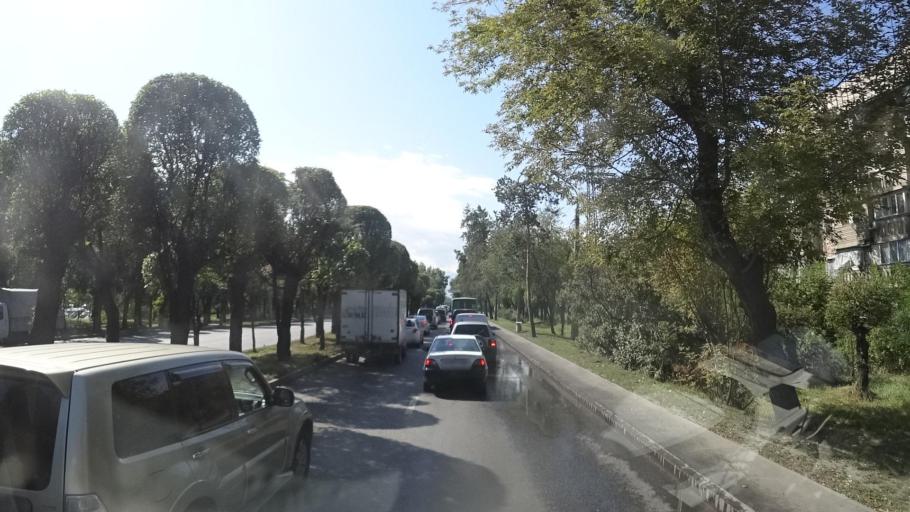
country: KZ
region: Almaty Oblysy
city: Pervomayskiy
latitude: 43.3244
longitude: 76.9743
